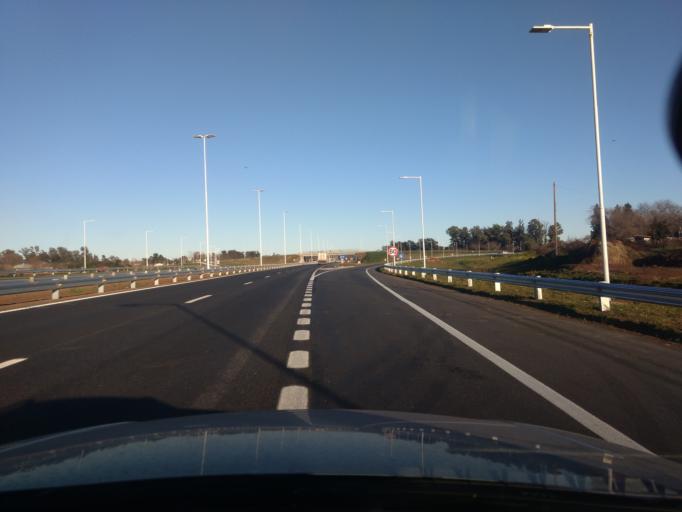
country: AR
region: Buenos Aires
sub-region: Partido de Lujan
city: Lujan
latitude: -34.5892
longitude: -59.0999
